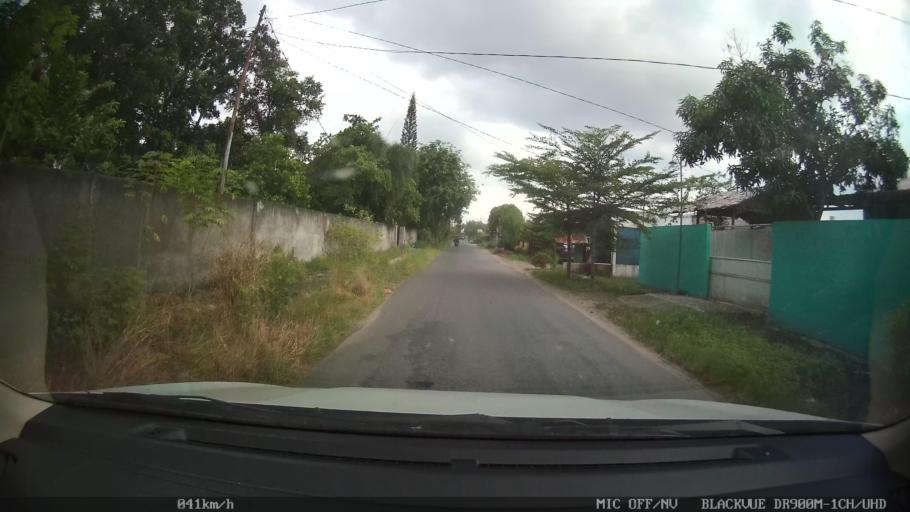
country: ID
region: North Sumatra
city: Sunggal
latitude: 3.6265
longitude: 98.6061
